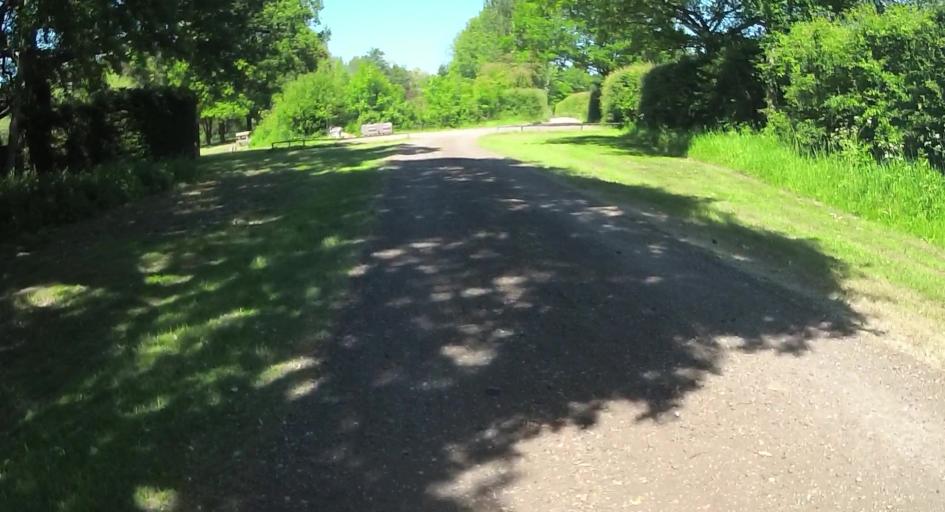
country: GB
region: England
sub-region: West Berkshire
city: Stratfield Mortimer
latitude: 51.3423
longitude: -1.0080
